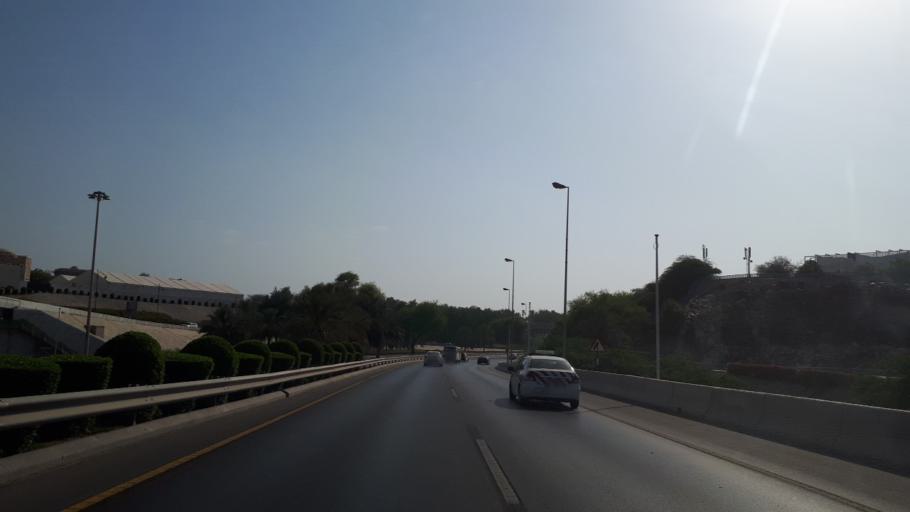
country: OM
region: Muhafazat Masqat
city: Bawshar
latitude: 23.6147
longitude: 58.4862
